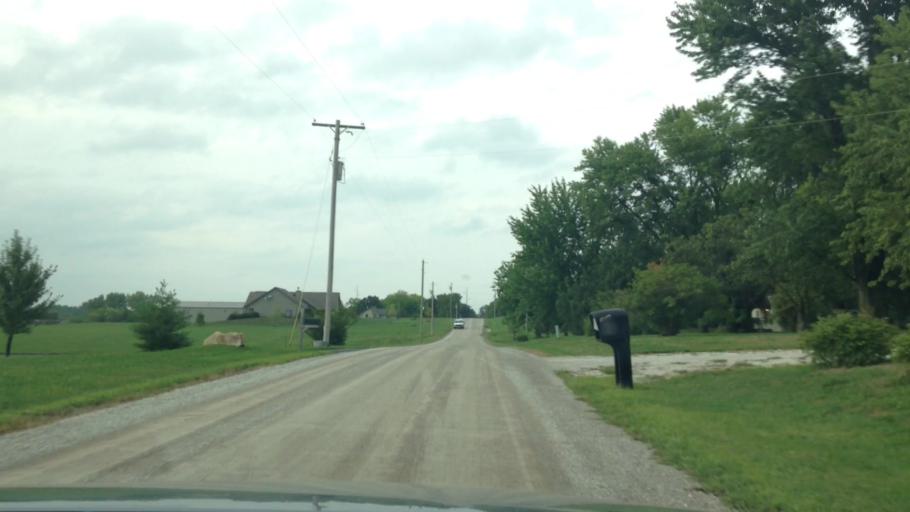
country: US
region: Missouri
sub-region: Clay County
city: Smithville
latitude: 39.4004
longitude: -94.6435
